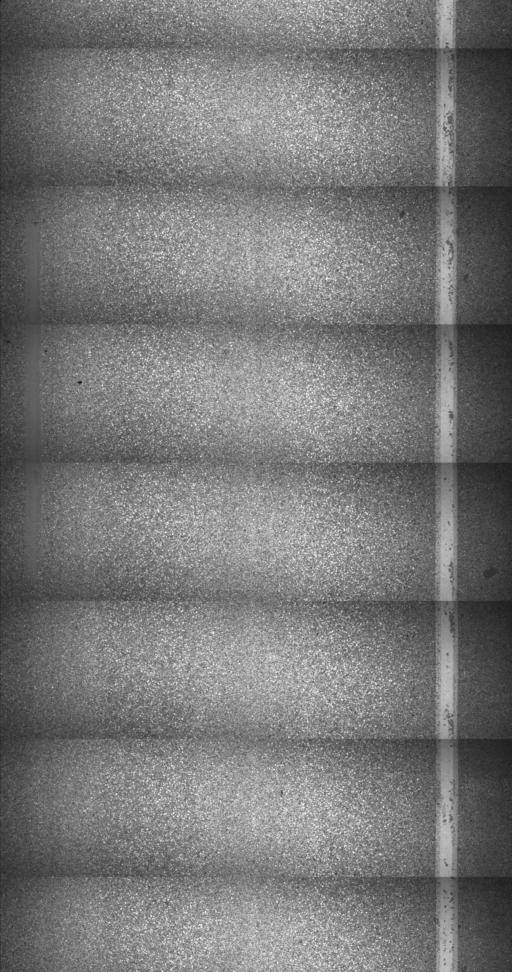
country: US
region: Vermont
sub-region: Franklin County
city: Enosburg Falls
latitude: 44.8484
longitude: -72.8057
